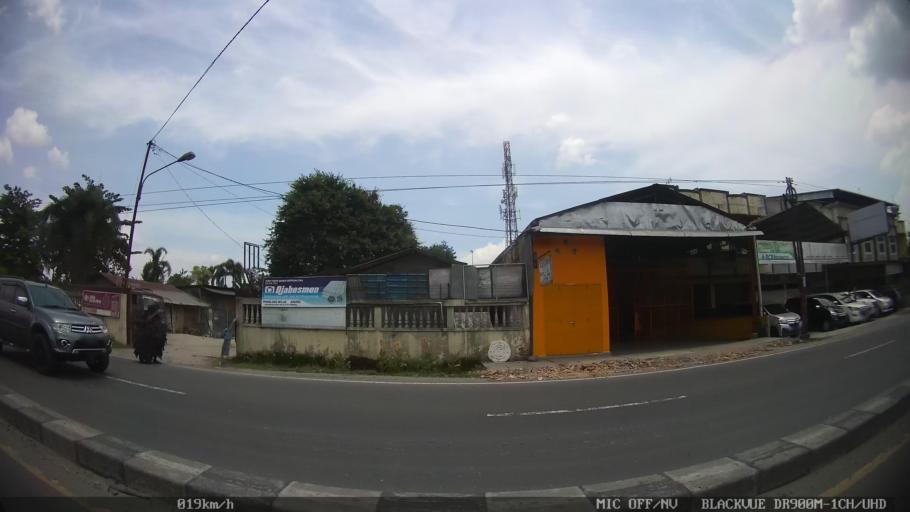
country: ID
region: North Sumatra
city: Binjai
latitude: 3.6010
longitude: 98.5472
